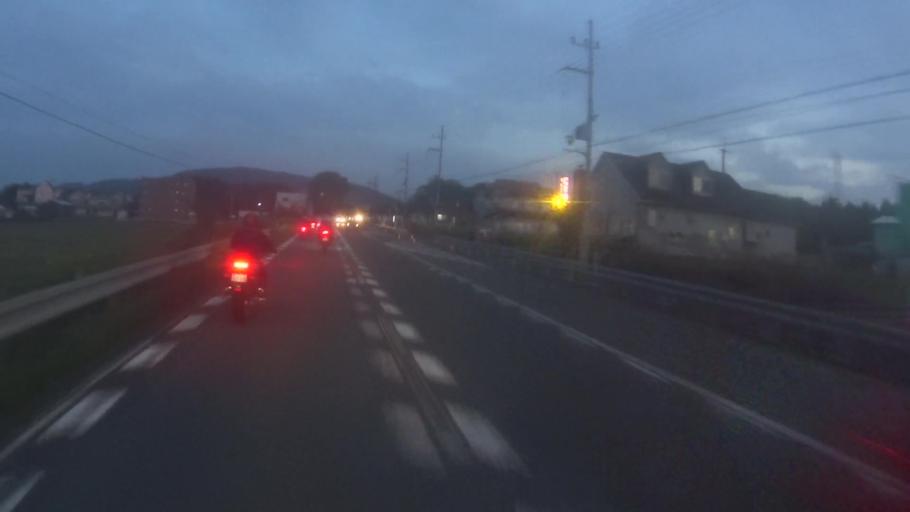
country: JP
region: Kyoto
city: Ayabe
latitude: 35.1752
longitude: 135.4234
